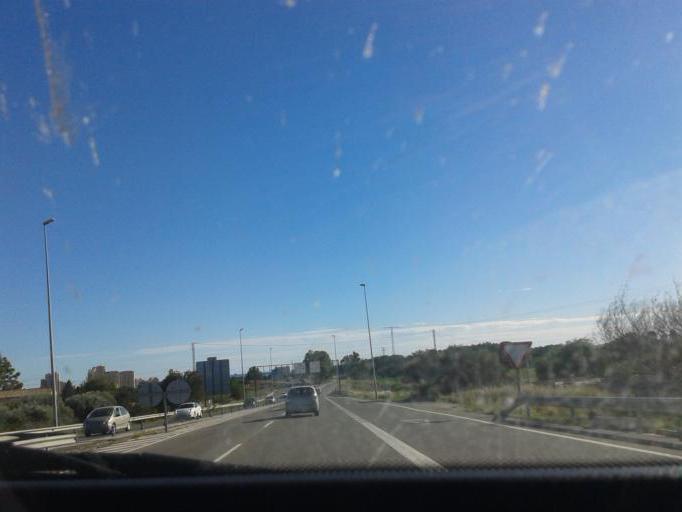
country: ES
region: Valencia
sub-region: Provincia de Alicante
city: San Juan de Alicante
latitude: 38.4178
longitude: -0.4246
